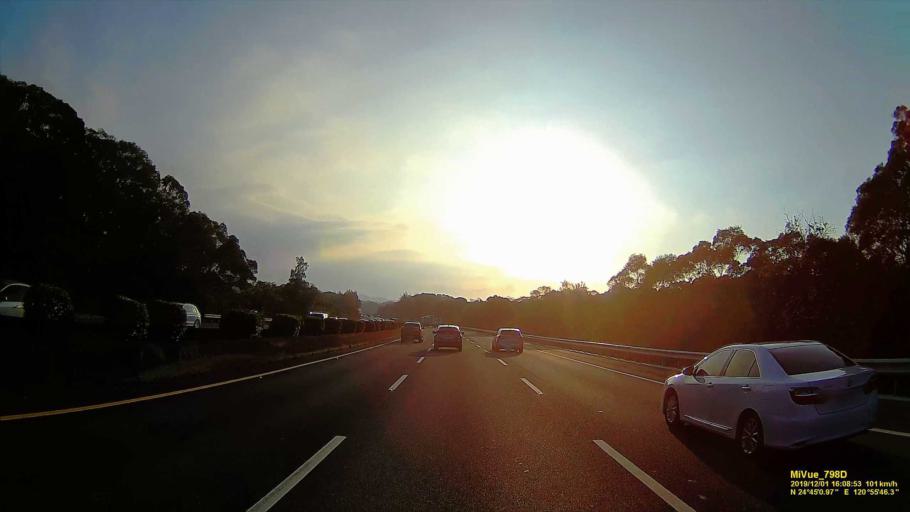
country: TW
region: Taiwan
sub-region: Hsinchu
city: Hsinchu
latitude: 24.7500
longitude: 120.9292
